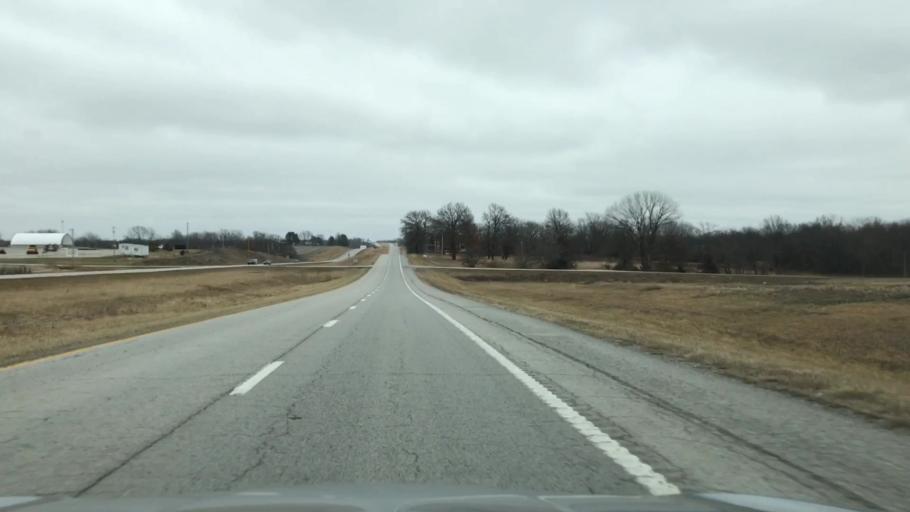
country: US
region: Missouri
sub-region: Linn County
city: Brookfield
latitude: 39.7784
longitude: -93.1683
